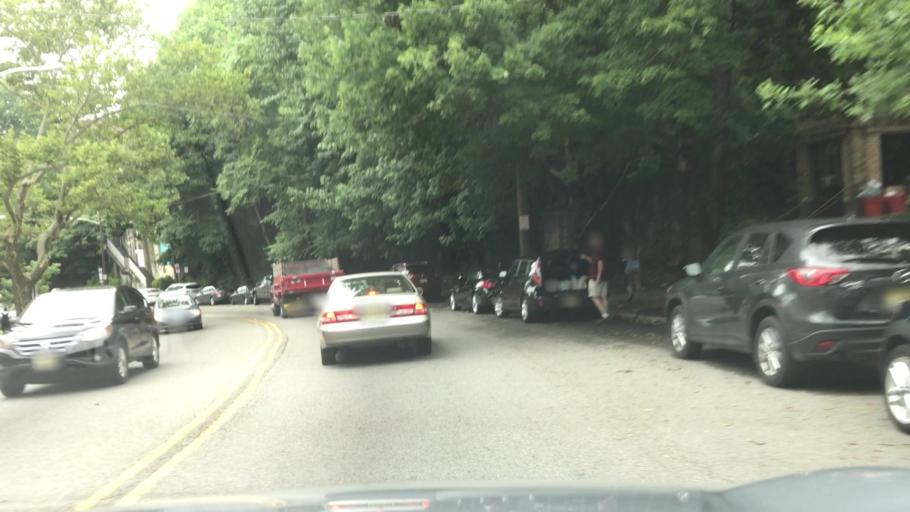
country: US
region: New Jersey
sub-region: Hudson County
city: Weehawken
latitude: 40.7710
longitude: -74.0204
